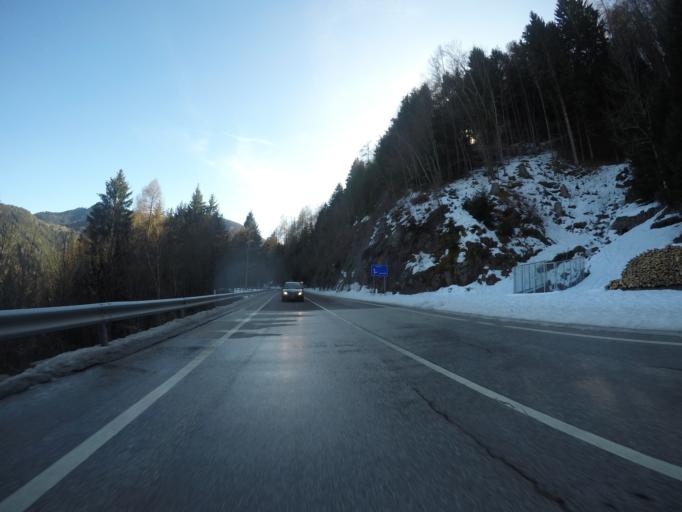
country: IT
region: Trentino-Alto Adige
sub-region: Provincia di Trento
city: Capriana
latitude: 46.2646
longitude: 11.3424
